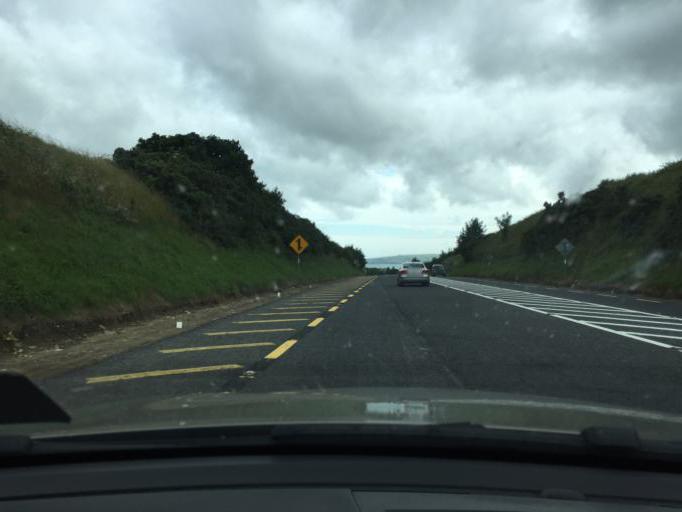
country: IE
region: Munster
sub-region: Waterford
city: Dungarvan
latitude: 52.1259
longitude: -7.5635
